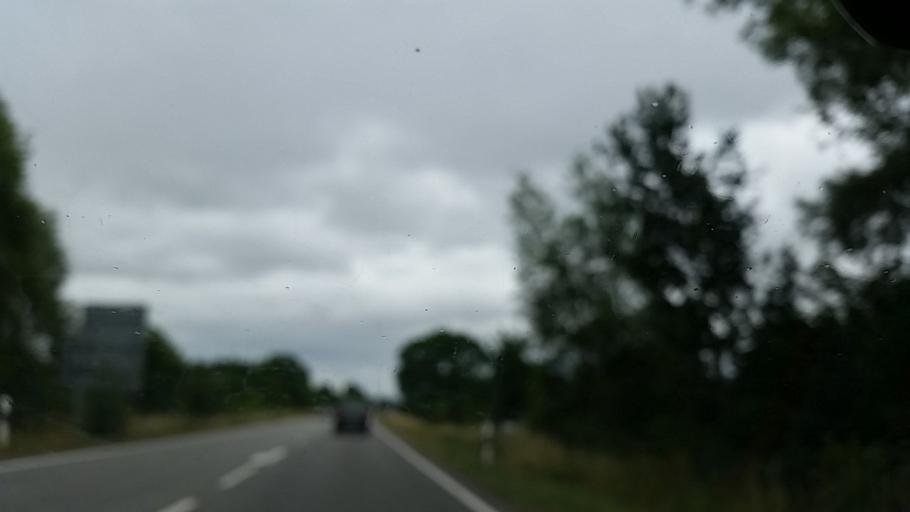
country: DE
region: Schleswig-Holstein
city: Tuttendorf
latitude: 54.4114
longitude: 9.9960
